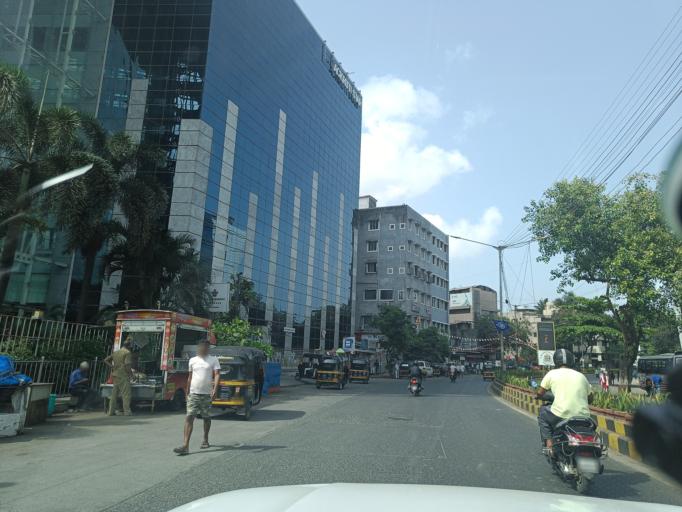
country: IN
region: Maharashtra
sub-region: Mumbai Suburban
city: Powai
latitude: 19.1190
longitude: 72.8703
